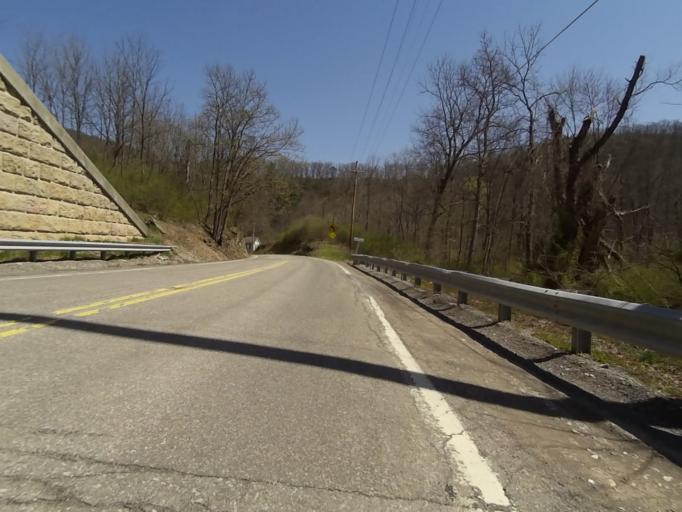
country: US
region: Pennsylvania
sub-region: Blair County
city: Williamsburg
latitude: 40.5694
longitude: -78.1417
